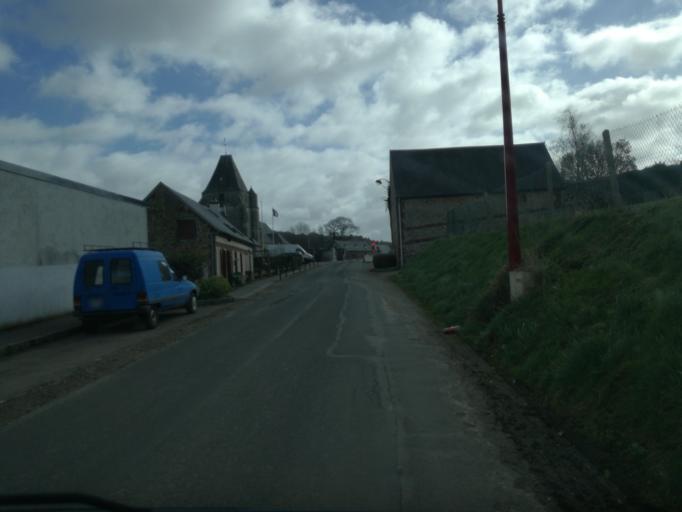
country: FR
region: Haute-Normandie
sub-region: Departement de la Seine-Maritime
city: Bretteville-du-Grand-Caux
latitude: 49.7033
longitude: 0.4481
